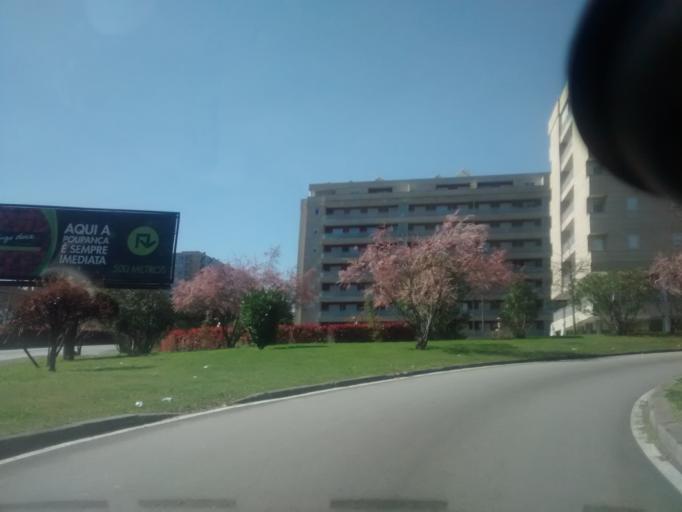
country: PT
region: Braga
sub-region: Braga
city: Braga
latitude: 41.5412
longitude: -8.4039
